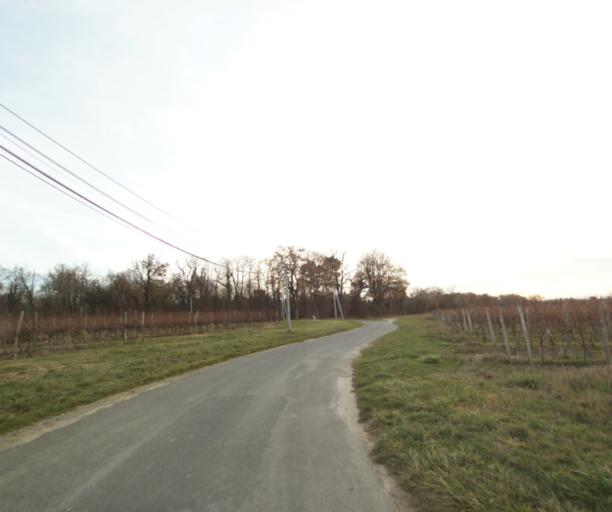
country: FR
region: Poitou-Charentes
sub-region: Departement de la Charente-Maritime
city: Fontcouverte
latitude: 45.7885
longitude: -0.5838
